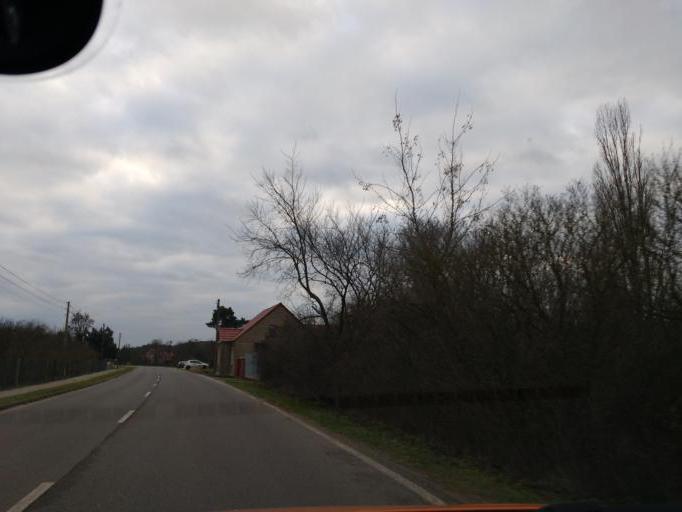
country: DE
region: Brandenburg
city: Wriezen
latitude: 52.7051
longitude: 14.1327
